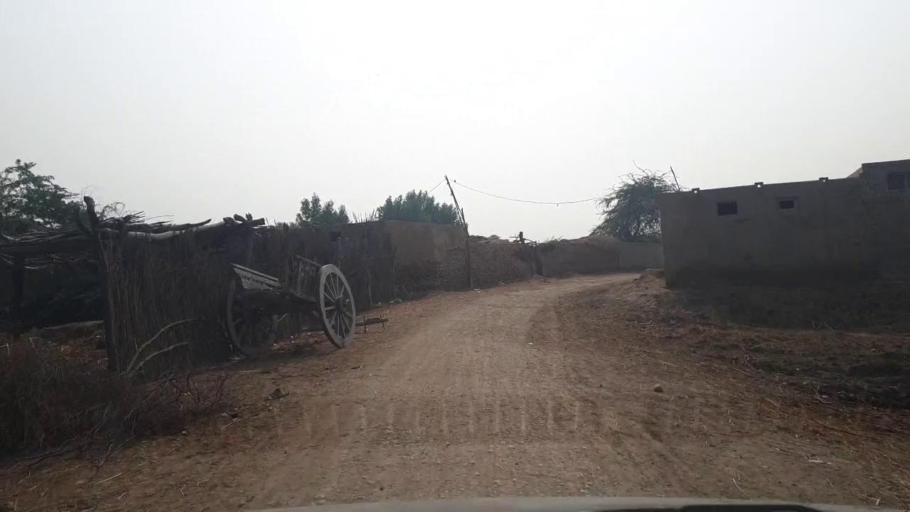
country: PK
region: Sindh
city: Tando Muhammad Khan
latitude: 25.2730
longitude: 68.4913
